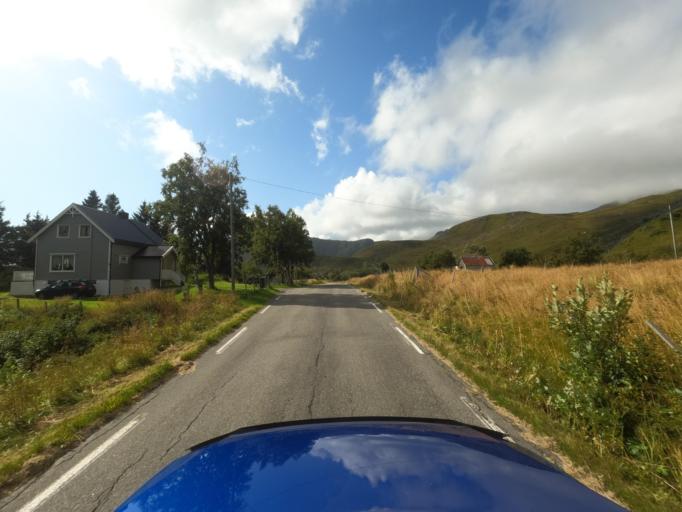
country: NO
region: Nordland
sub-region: Vestvagoy
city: Evjen
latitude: 68.2173
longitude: 14.0606
